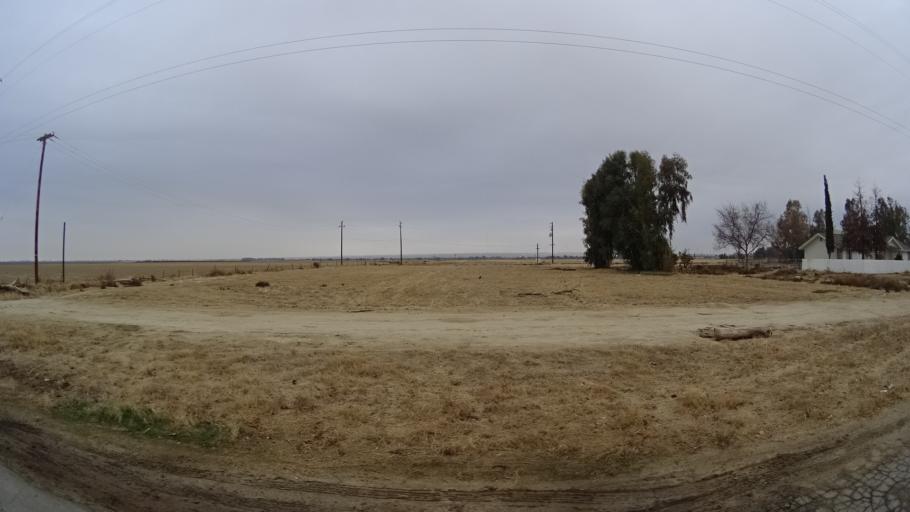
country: US
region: California
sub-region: Kern County
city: Lamont
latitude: 35.3251
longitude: -118.9407
